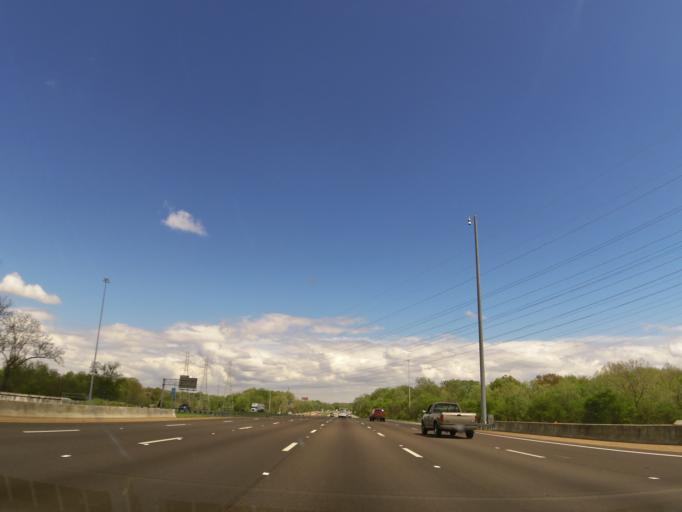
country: US
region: Tennessee
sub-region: Shelby County
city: Memphis
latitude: 35.1916
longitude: -90.0083
